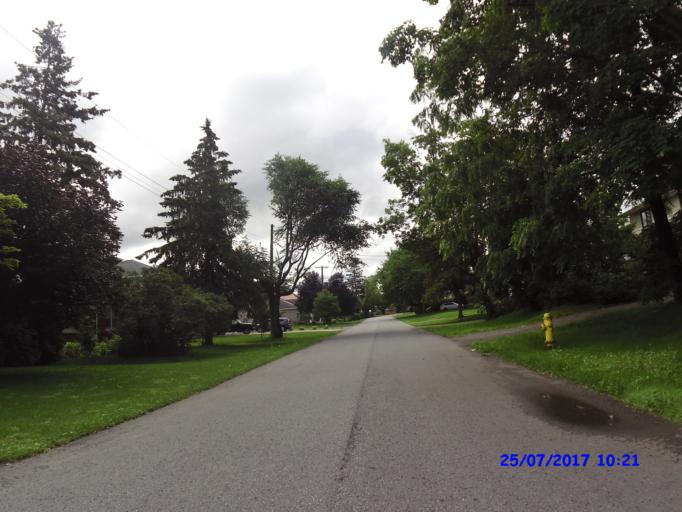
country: CA
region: Ontario
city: Ottawa
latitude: 45.3622
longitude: -75.7093
